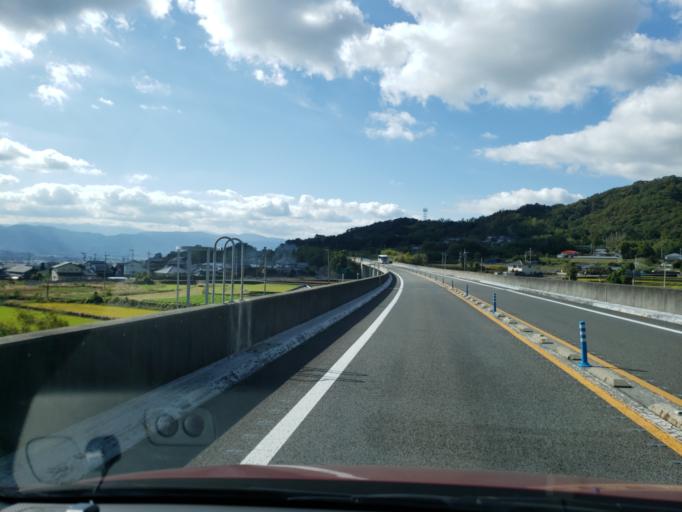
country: JP
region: Tokushima
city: Ishii
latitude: 34.1356
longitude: 134.3966
